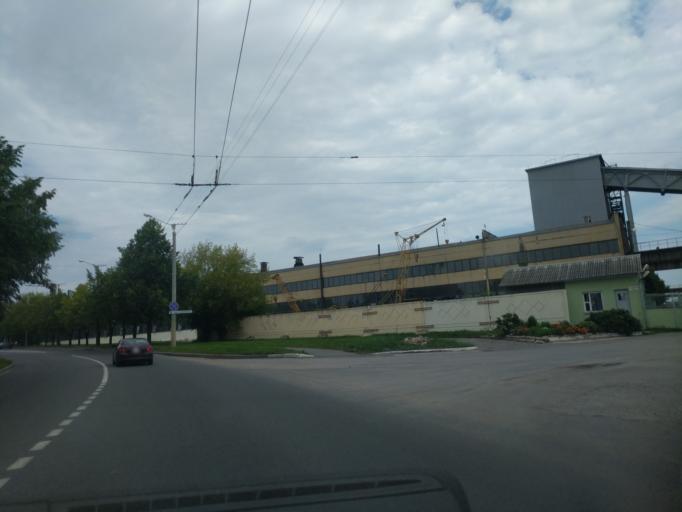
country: BY
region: Minsk
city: Novoye Medvezhino
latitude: 53.8913
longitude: 27.4833
